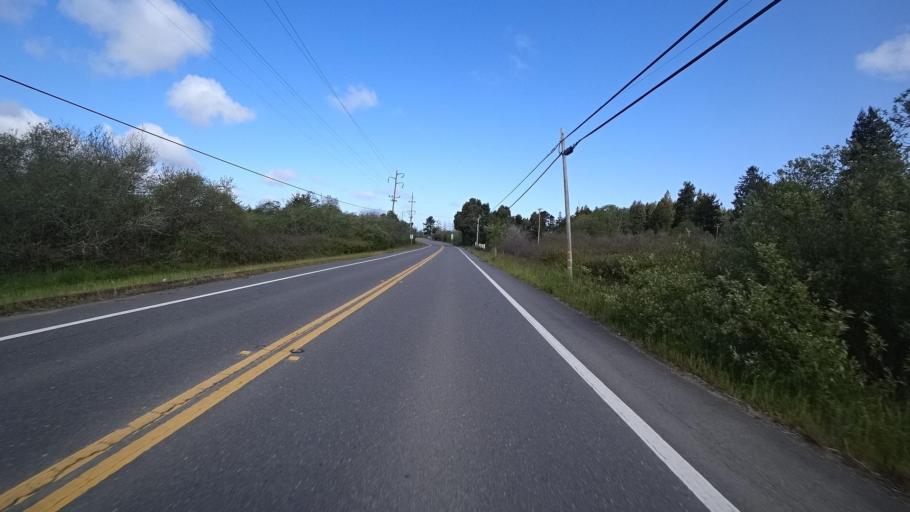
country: US
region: California
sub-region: Humboldt County
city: Myrtletown
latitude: 40.7836
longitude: -124.0801
